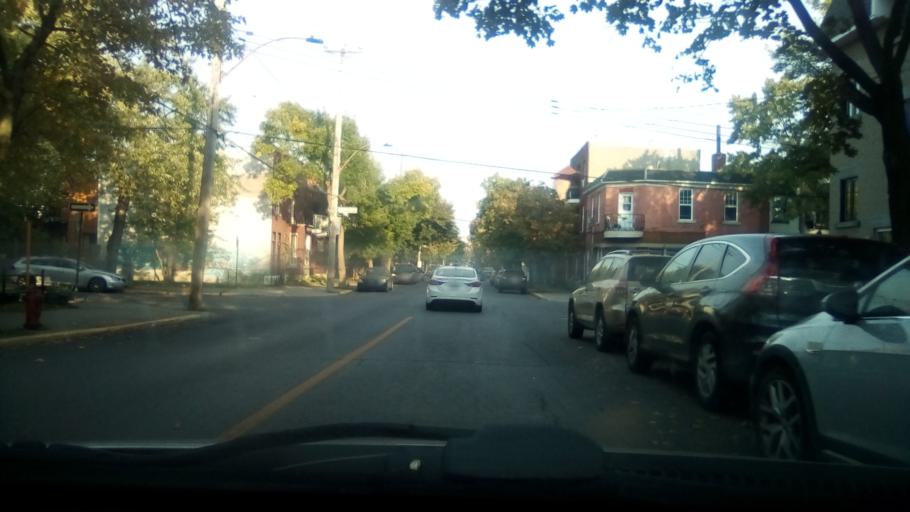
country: CA
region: Quebec
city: Westmount
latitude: 45.4746
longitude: -73.5622
